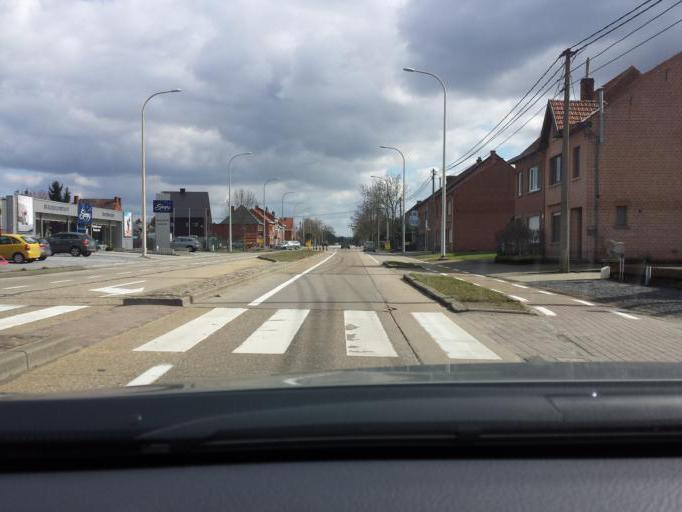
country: BE
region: Flanders
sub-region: Provincie Vlaams-Brabant
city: Diest
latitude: 50.9722
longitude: 5.0706
